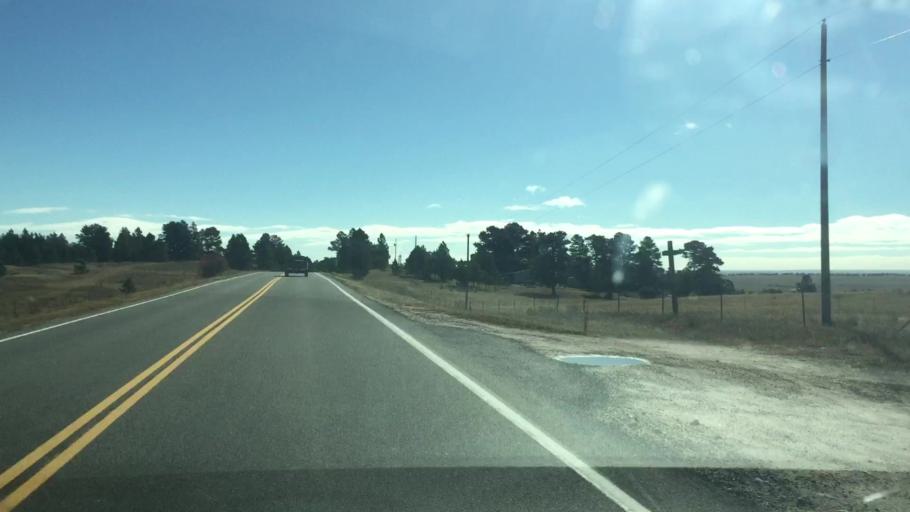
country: US
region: Colorado
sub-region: Elbert County
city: Kiowa
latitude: 39.3322
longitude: -104.4150
